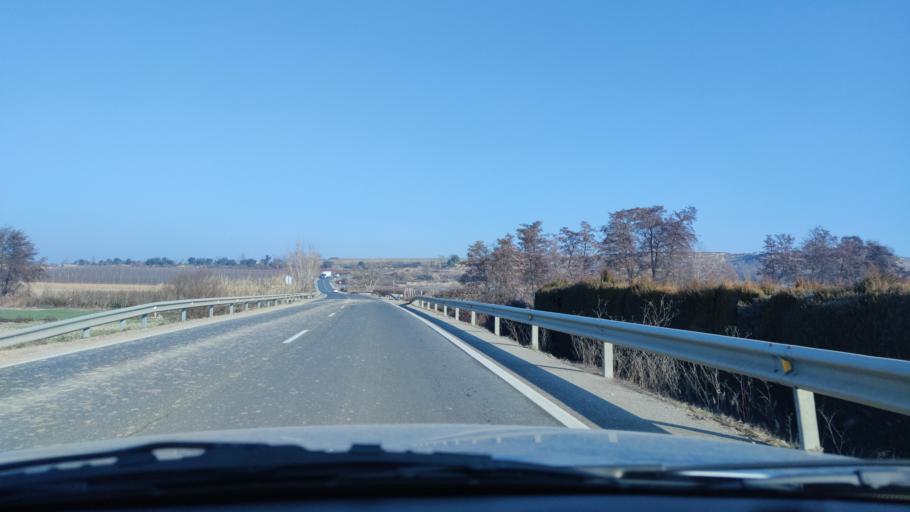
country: ES
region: Catalonia
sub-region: Provincia de Lleida
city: Albesa
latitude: 41.7228
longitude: 0.6402
